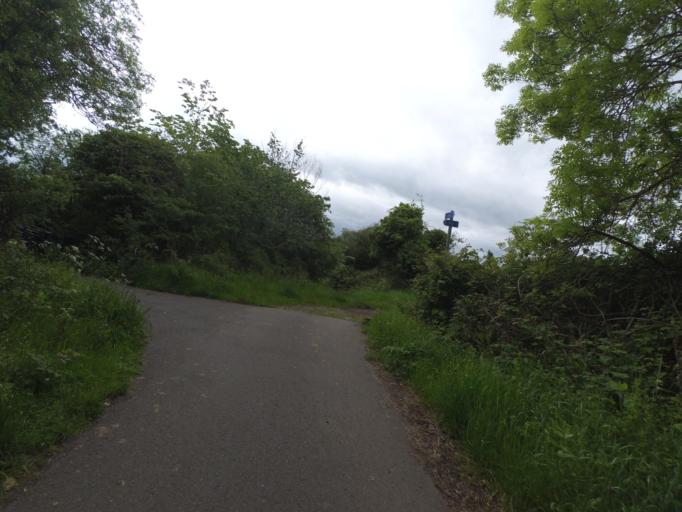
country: GB
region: Scotland
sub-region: East Lothian
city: Musselburgh
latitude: 55.9280
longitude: -3.0513
